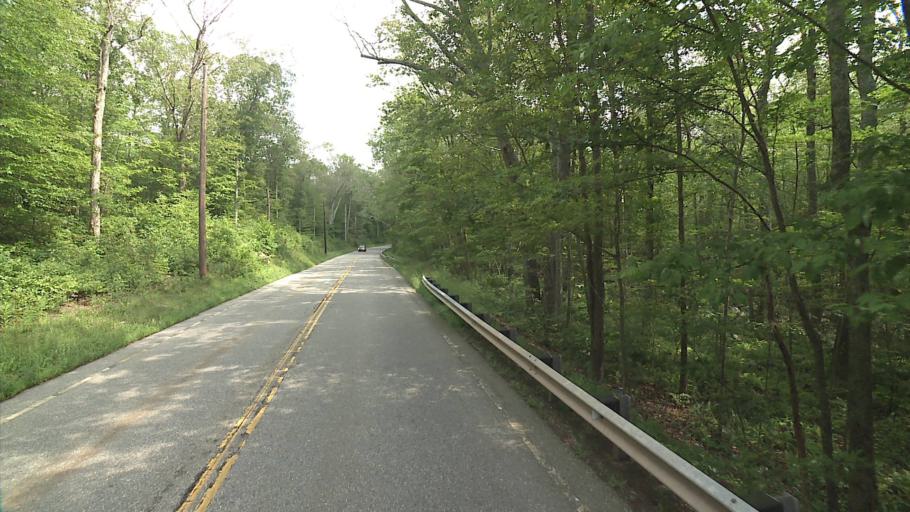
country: US
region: Connecticut
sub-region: New London County
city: Colchester
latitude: 41.4546
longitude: -72.3075
